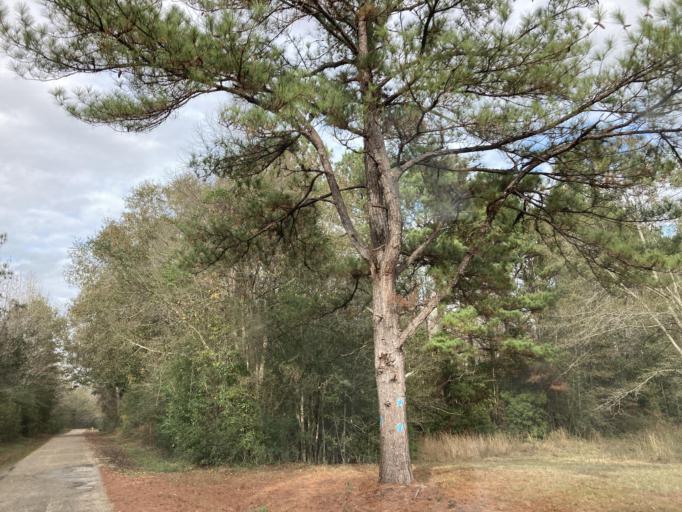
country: US
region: Mississippi
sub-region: Lamar County
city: Lumberton
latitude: 30.9944
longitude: -89.2648
